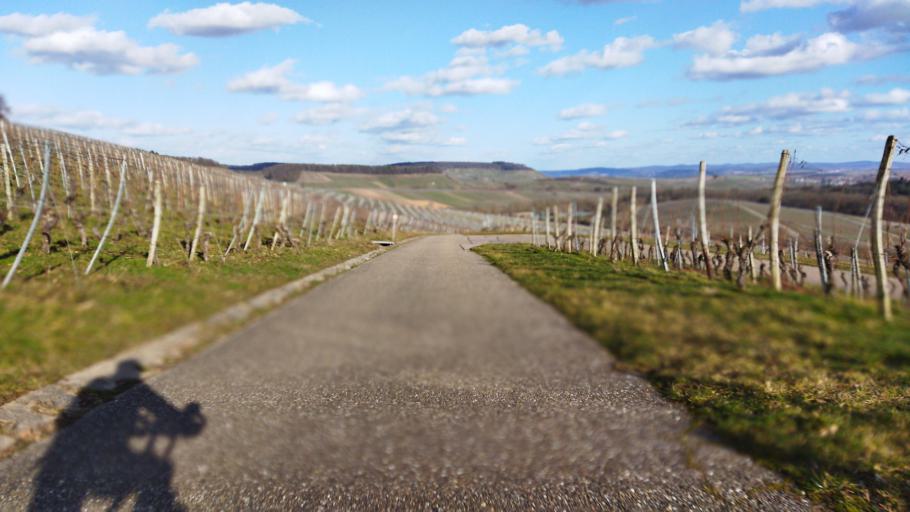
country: DE
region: Baden-Wuerttemberg
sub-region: Regierungsbezirk Stuttgart
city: Guglingen
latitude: 49.0914
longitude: 9.0146
